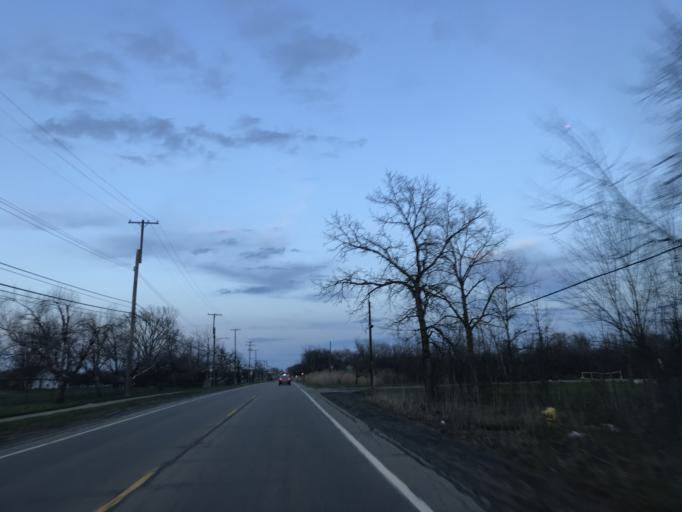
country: US
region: Michigan
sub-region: Wayne County
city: Riverview
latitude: 42.1701
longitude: -83.2024
